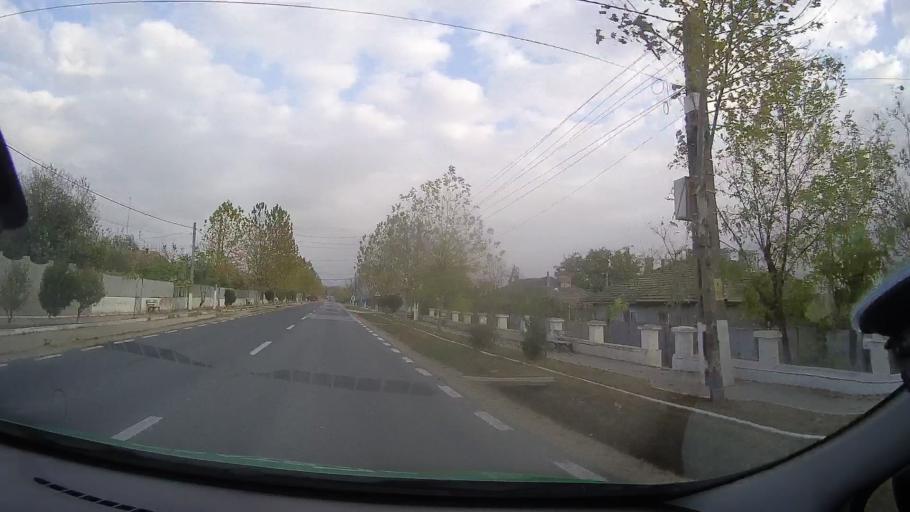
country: RO
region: Constanta
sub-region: Comuna Mircea Voda
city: Satu Nou
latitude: 44.2691
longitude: 28.2183
